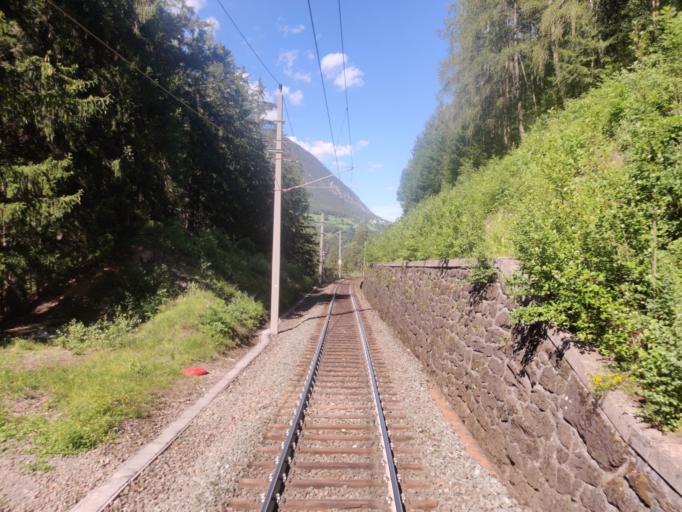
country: AT
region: Tyrol
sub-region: Politischer Bezirk Landeck
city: Pians
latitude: 47.1332
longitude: 10.5203
